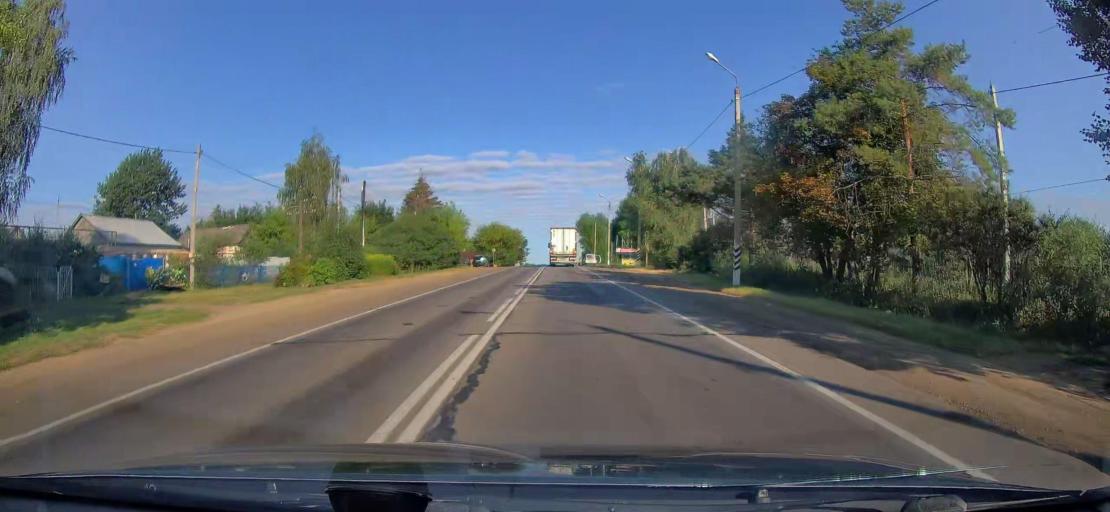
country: RU
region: Tula
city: Chern'
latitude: 53.4529
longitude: 36.8780
